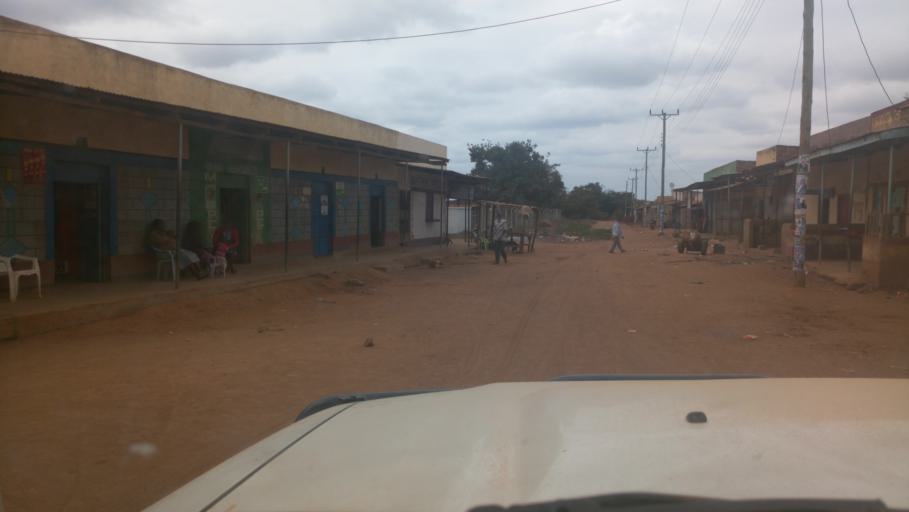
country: KE
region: Makueni
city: Wote
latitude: -1.7596
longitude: 37.9096
